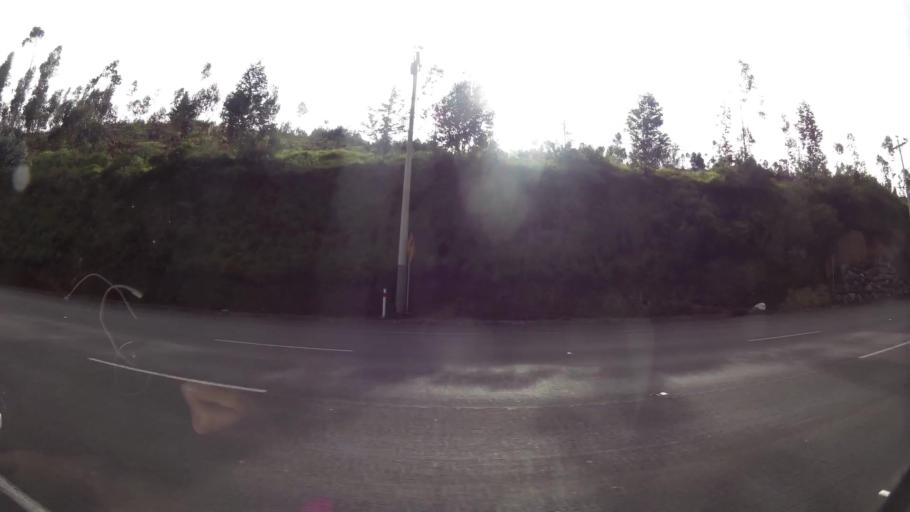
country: EC
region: Pichincha
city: Sangolqui
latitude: -0.3901
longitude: -78.5351
